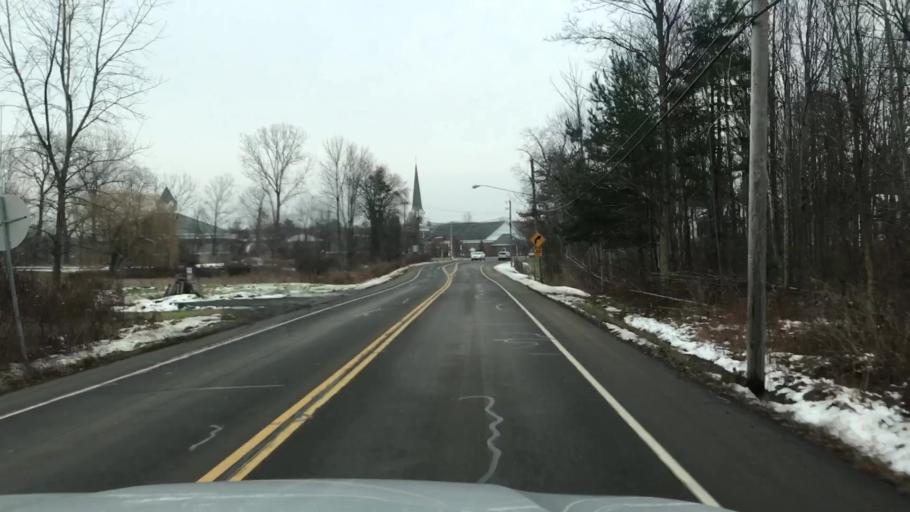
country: US
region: New York
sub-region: Erie County
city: Hamburg
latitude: 42.7515
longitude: -78.8148
